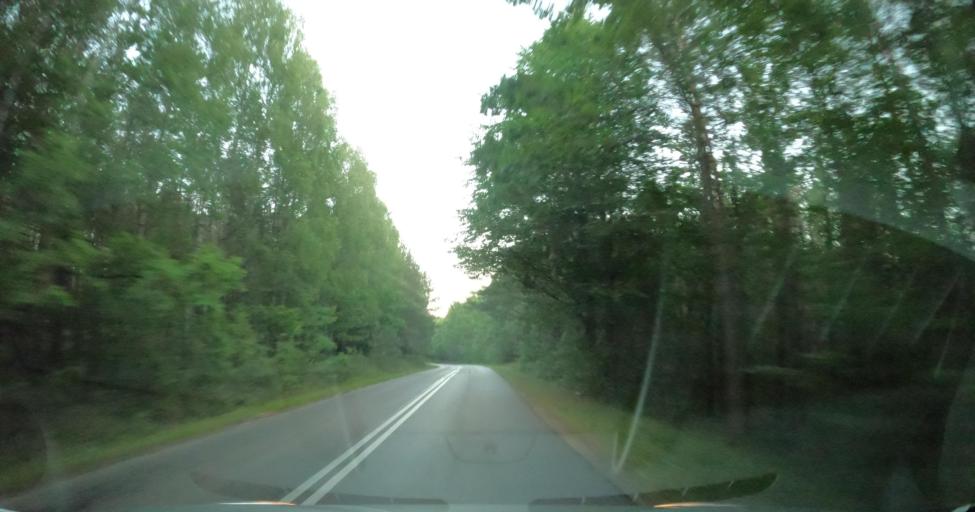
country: PL
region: Pomeranian Voivodeship
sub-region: Powiat wejherowski
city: Linia
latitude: 54.4619
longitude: 17.9972
